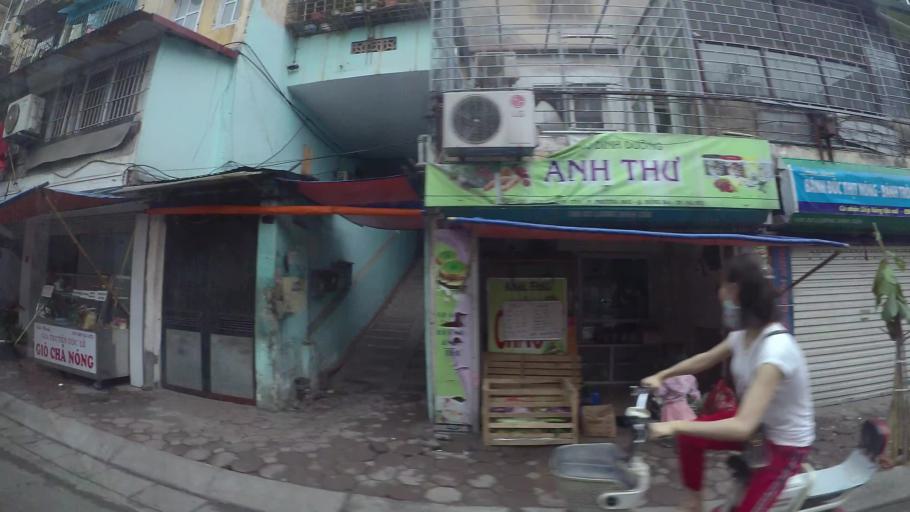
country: VN
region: Ha Noi
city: Hai BaTrung
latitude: 21.0025
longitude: 105.8361
